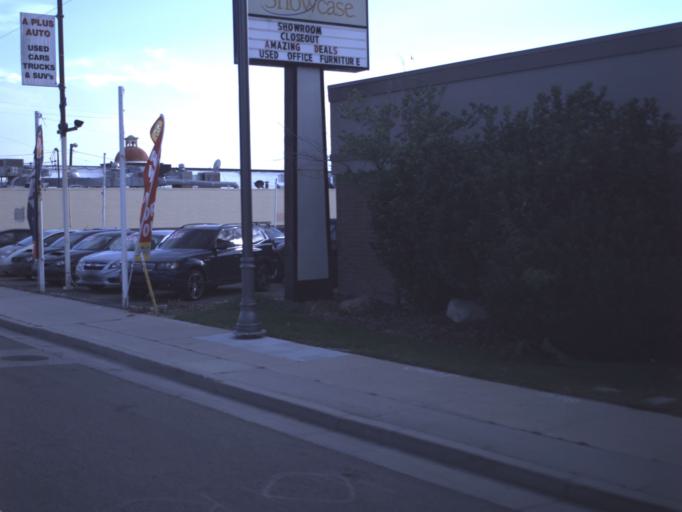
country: US
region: Utah
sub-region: Salt Lake County
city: Centerfield
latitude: 40.6935
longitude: -111.8884
